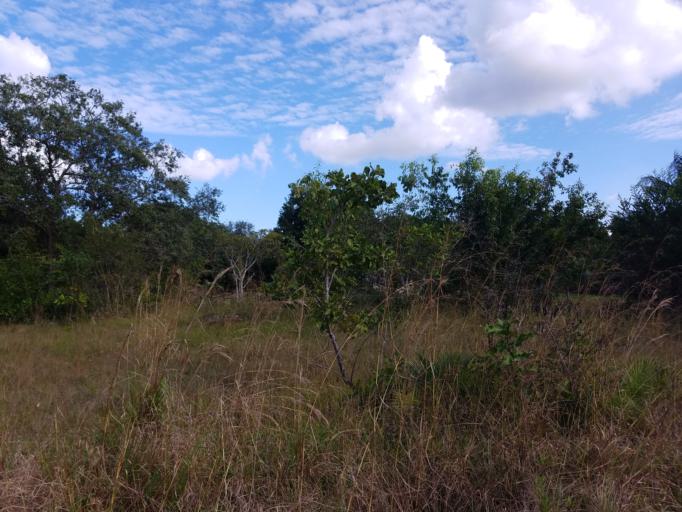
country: BZ
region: Belize
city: Belize City
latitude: 17.5673
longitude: -88.4109
